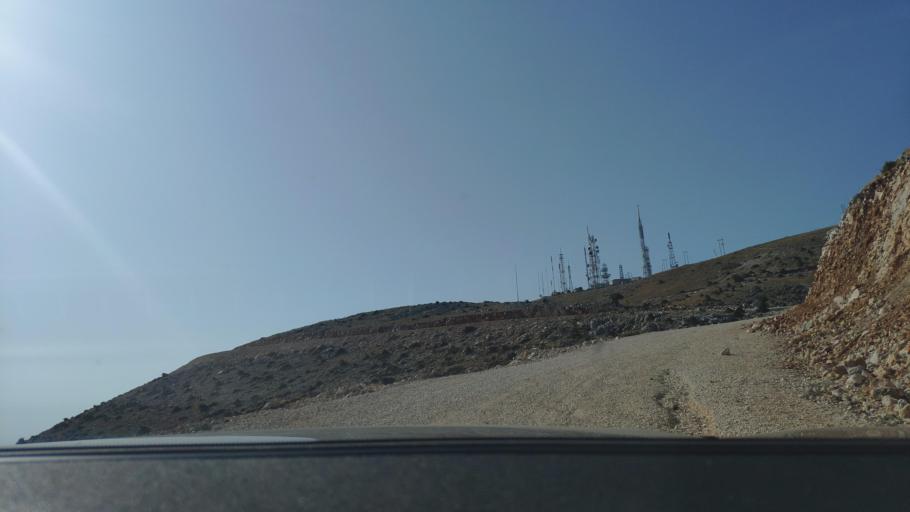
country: GR
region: West Greece
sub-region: Nomos Aitolias kai Akarnanias
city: Monastirakion
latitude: 38.8126
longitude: 20.9825
